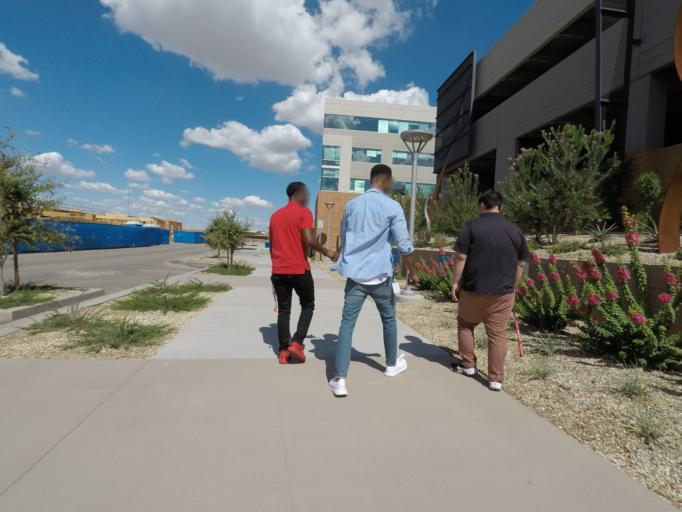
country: US
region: Arizona
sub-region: Maricopa County
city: Tempe
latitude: 33.4342
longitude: -111.8988
